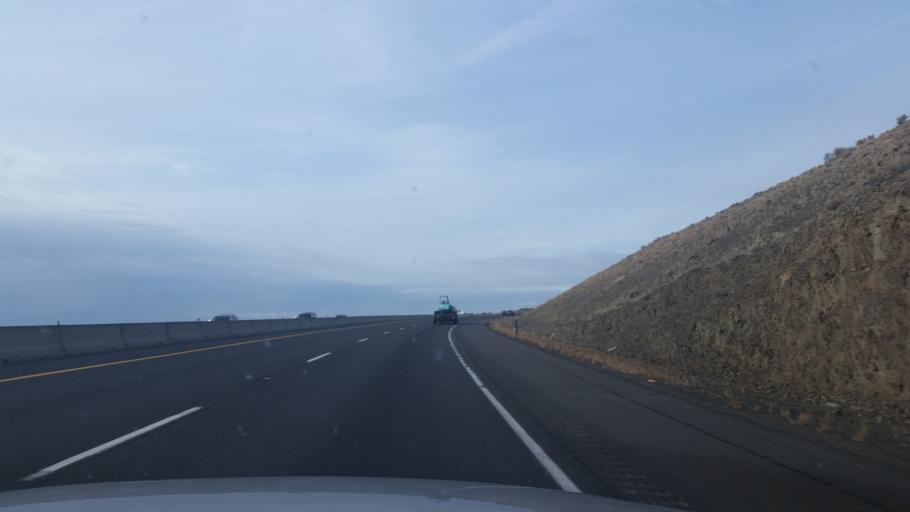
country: US
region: Washington
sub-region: Grant County
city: Mattawa
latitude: 46.9629
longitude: -119.9660
